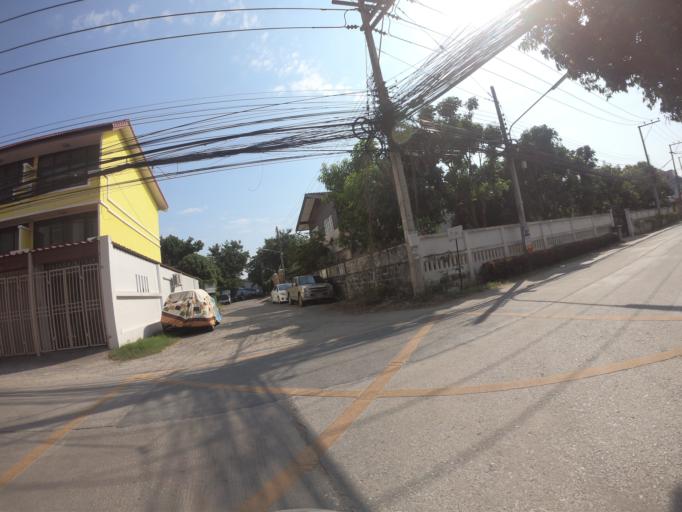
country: TH
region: Chiang Mai
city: Chiang Mai
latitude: 18.8068
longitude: 98.9928
